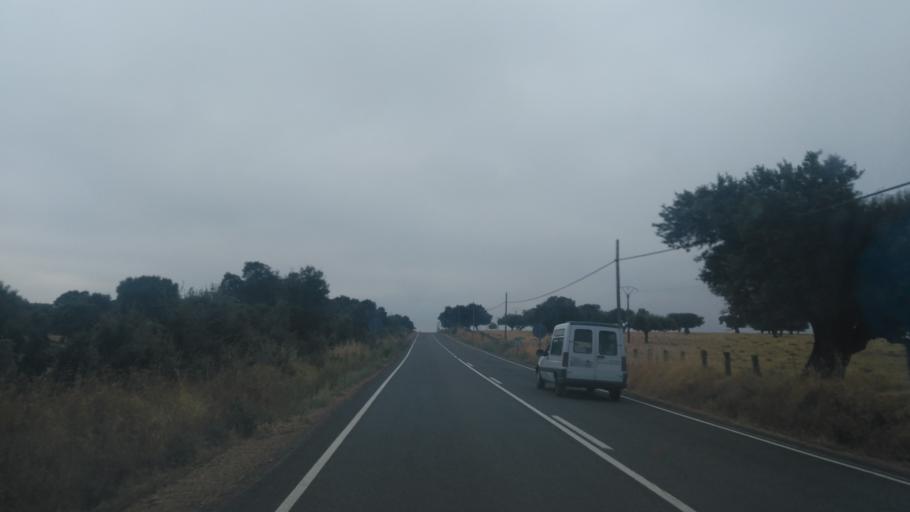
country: ES
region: Castille and Leon
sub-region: Provincia de Salamanca
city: Matilla de los Canos del Rio
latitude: 40.8471
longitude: -5.9566
